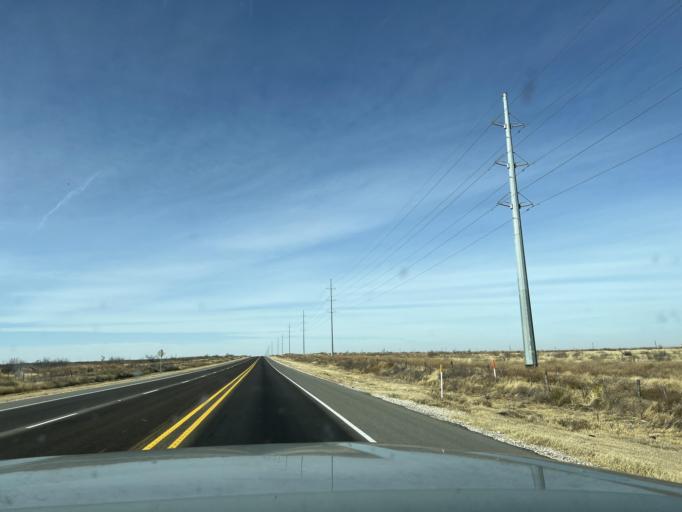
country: US
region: Texas
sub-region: Andrews County
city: Andrews
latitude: 32.3512
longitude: -102.7381
